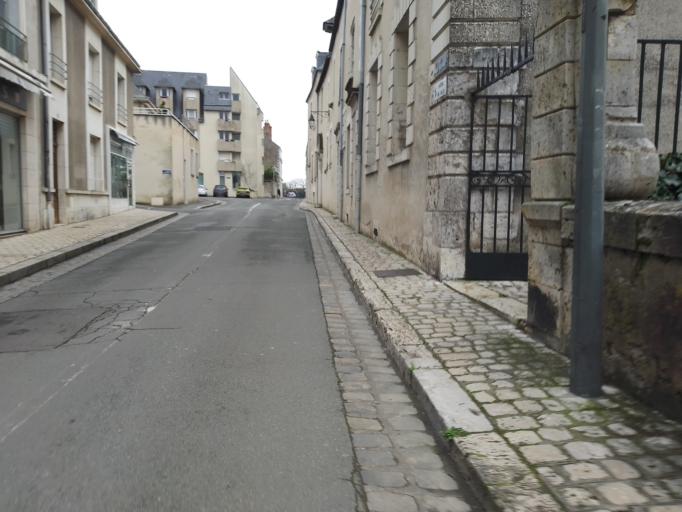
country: FR
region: Centre
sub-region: Departement du Loir-et-Cher
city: Blois
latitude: 47.5888
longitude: 1.3363
